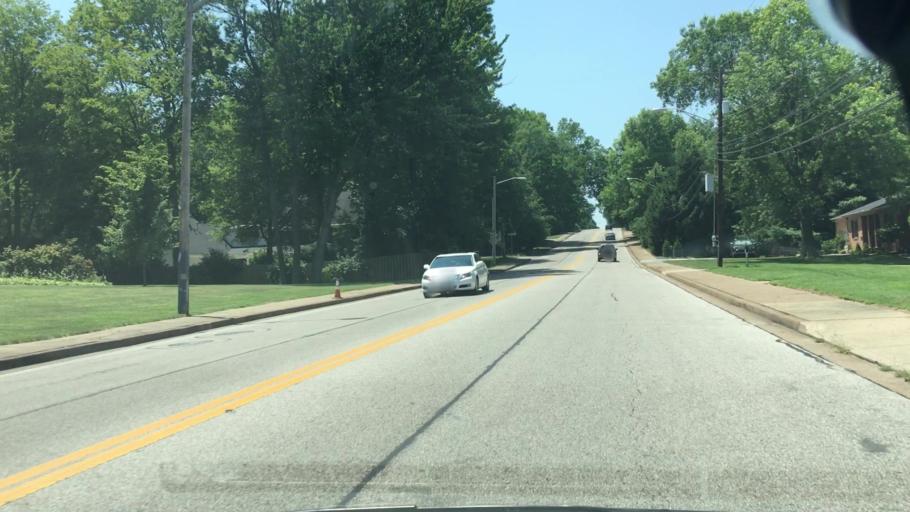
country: US
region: Indiana
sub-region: Vanderburgh County
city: Melody Hill
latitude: 37.9694
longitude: -87.4769
